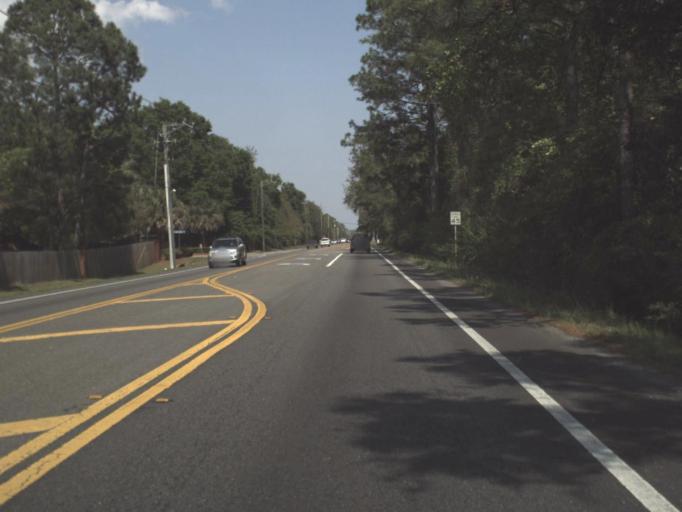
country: US
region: Florida
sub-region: Escambia County
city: Myrtle Grove
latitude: 30.3993
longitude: -87.3891
